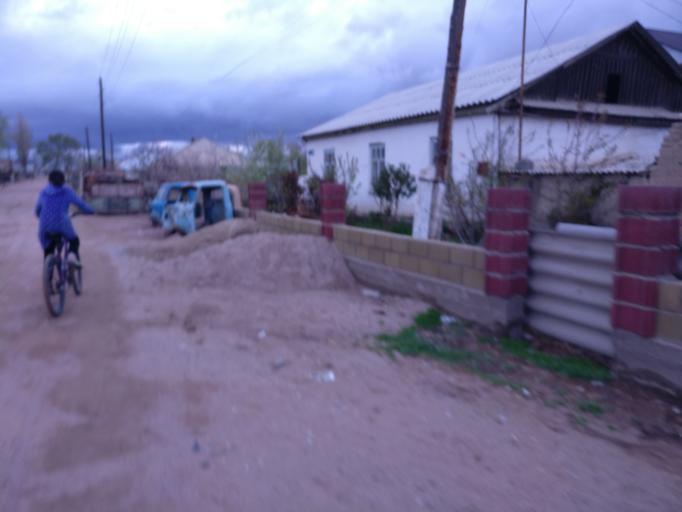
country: KG
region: Ysyk-Koel
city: Bokombayevskoye
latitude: 42.1161
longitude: 76.9910
